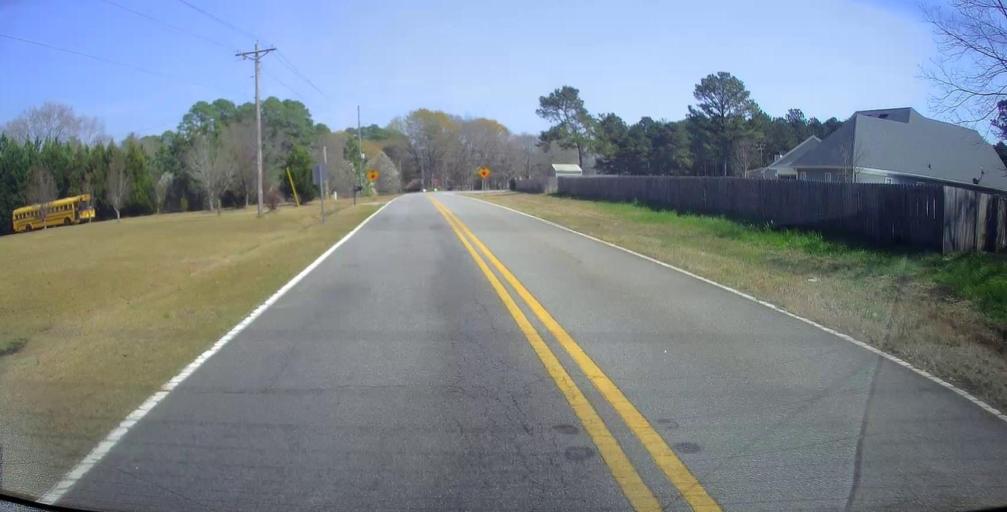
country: US
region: Georgia
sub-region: Houston County
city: Centerville
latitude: 32.5854
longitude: -83.6959
